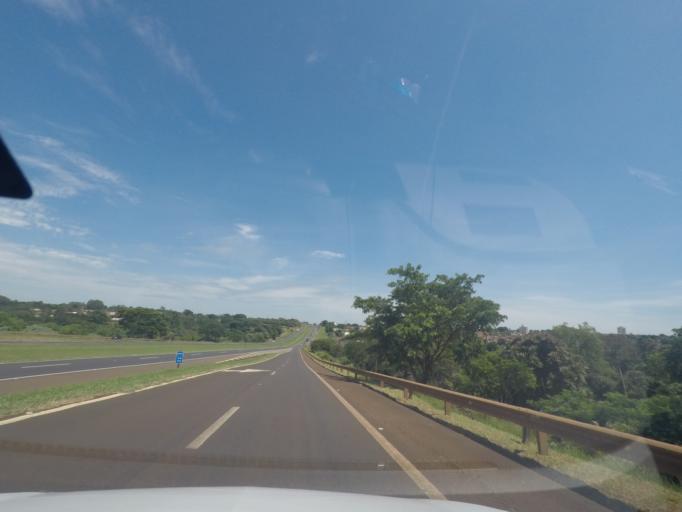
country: BR
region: Sao Paulo
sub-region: Araraquara
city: Araraquara
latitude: -21.8157
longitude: -48.1817
